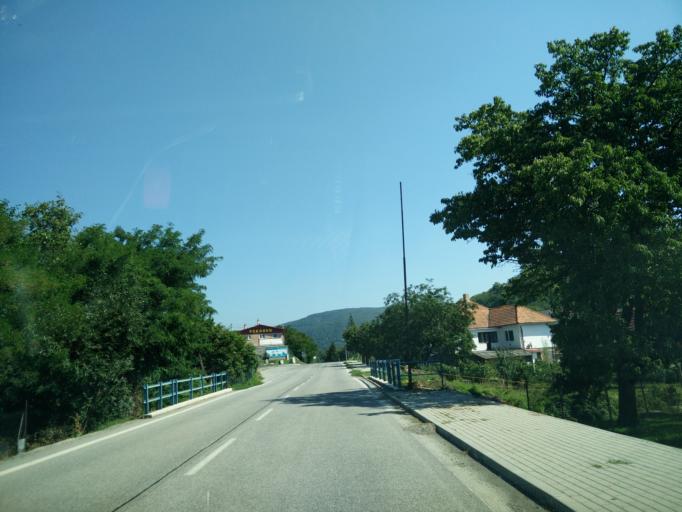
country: SK
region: Nitriansky
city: Tlmace
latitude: 48.3452
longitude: 18.5484
